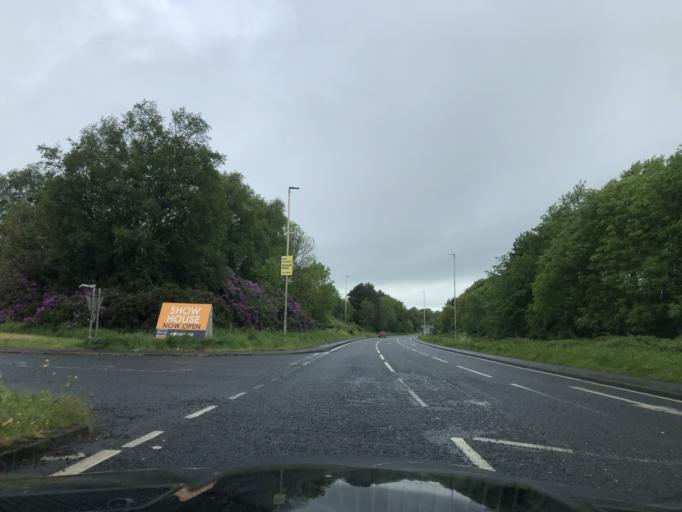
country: GB
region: Northern Ireland
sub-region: Ballymoney District
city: Ballymoney
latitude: 55.0656
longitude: -6.4837
